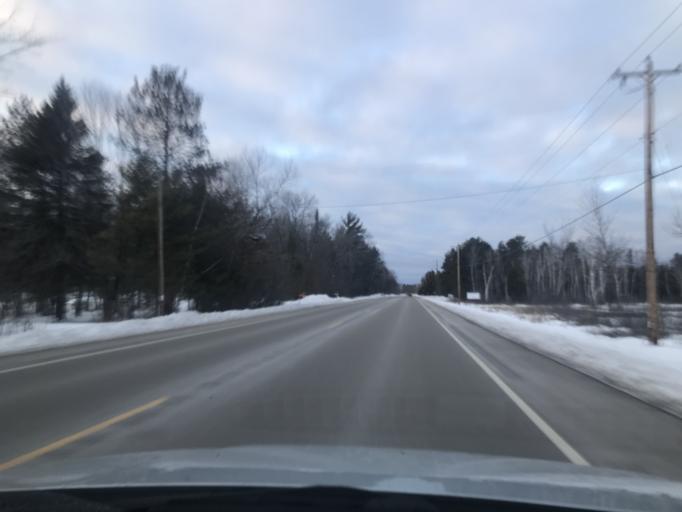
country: US
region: Wisconsin
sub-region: Marinette County
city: Marinette
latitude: 45.1317
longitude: -87.6876
